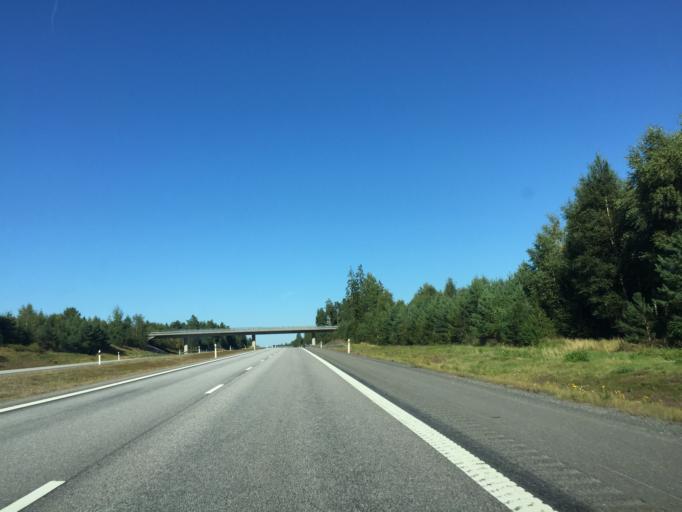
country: SE
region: OErebro
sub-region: Lindesbergs Kommun
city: Fellingsbro
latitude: 59.3387
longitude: 15.5394
